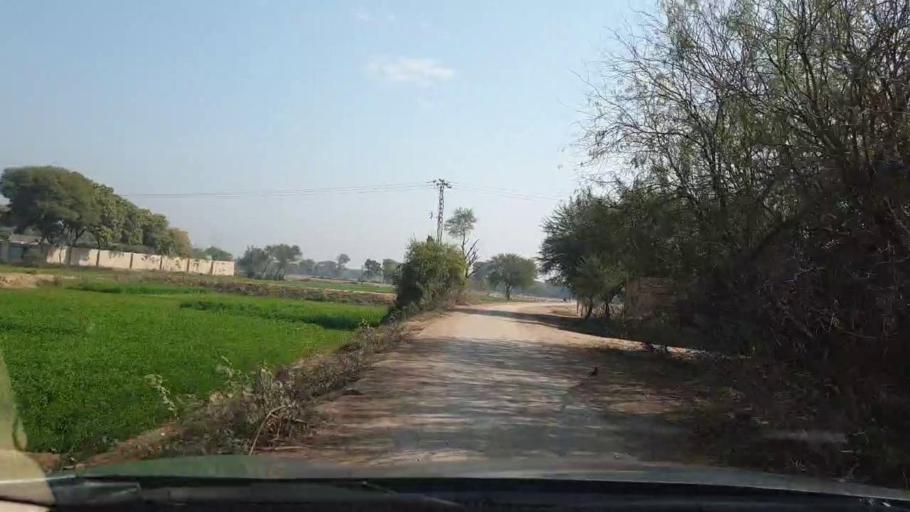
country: PK
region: Sindh
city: Tando Allahyar
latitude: 25.4635
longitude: 68.6685
